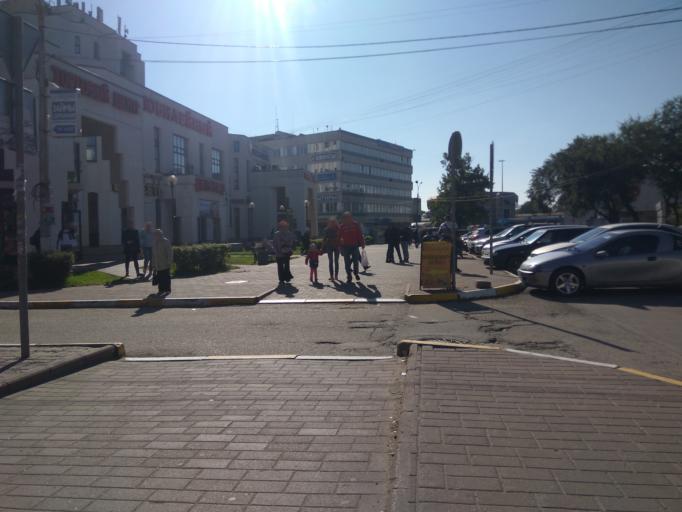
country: RU
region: Moskovskaya
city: Ramenskoye
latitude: 55.5670
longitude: 38.2282
